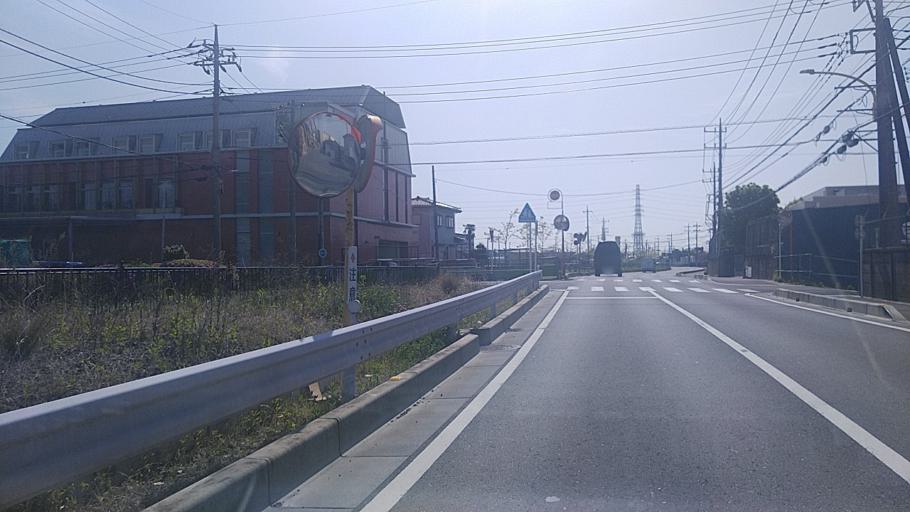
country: JP
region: Saitama
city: Koshigaya
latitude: 35.8705
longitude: 139.7693
